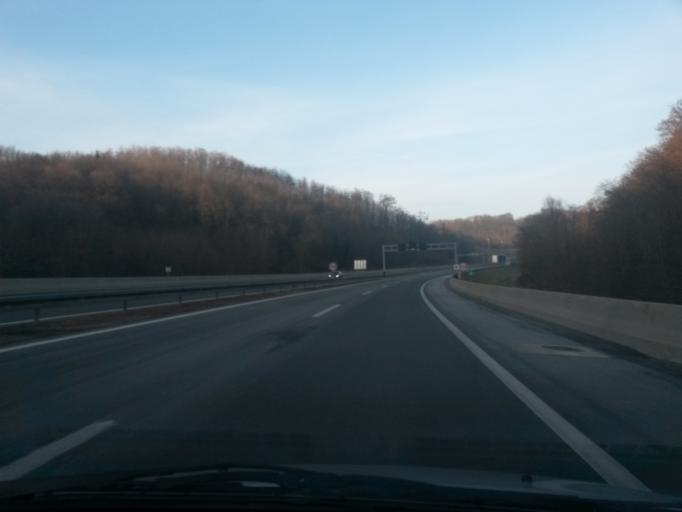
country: HR
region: Varazdinska
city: Ljubescica
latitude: 46.2151
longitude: 16.4043
